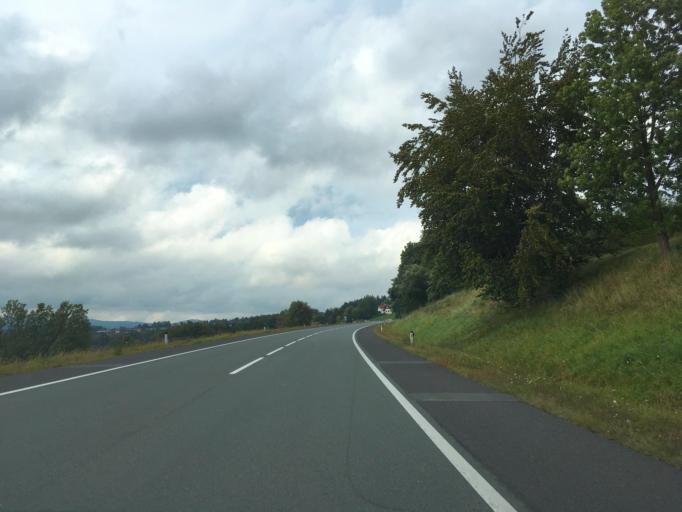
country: AT
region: Styria
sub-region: Politischer Bezirk Hartberg-Fuerstenfeld
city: Pinggau
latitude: 47.4441
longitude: 16.0756
